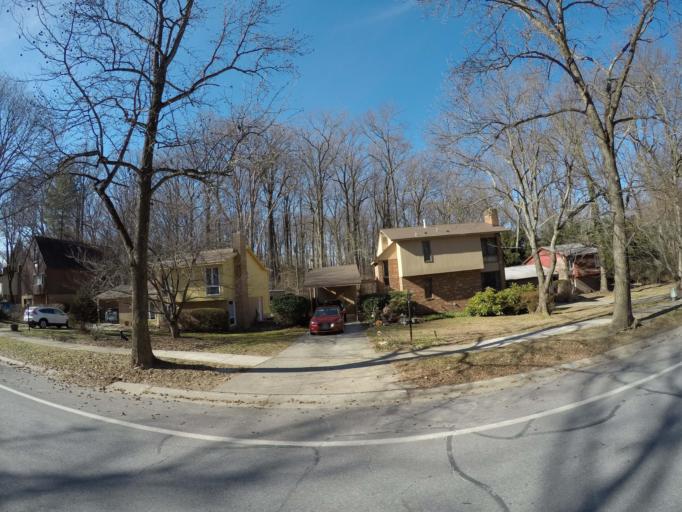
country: US
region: Maryland
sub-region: Howard County
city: Columbia
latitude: 39.2232
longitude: -76.8320
